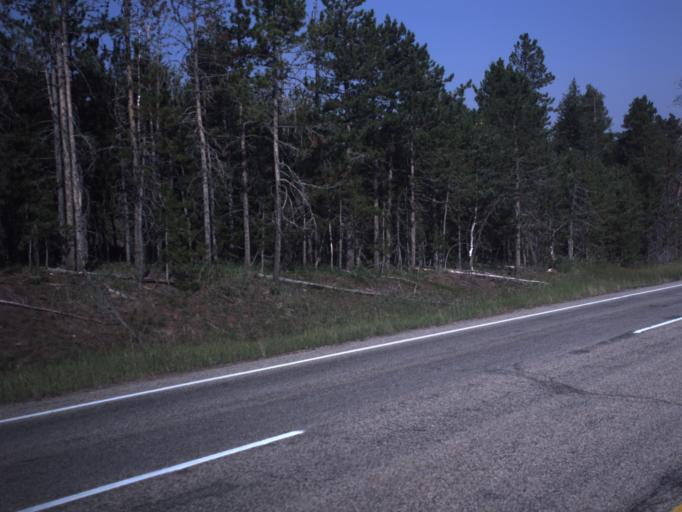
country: US
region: Utah
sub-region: Daggett County
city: Manila
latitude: 40.8570
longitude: -109.4647
